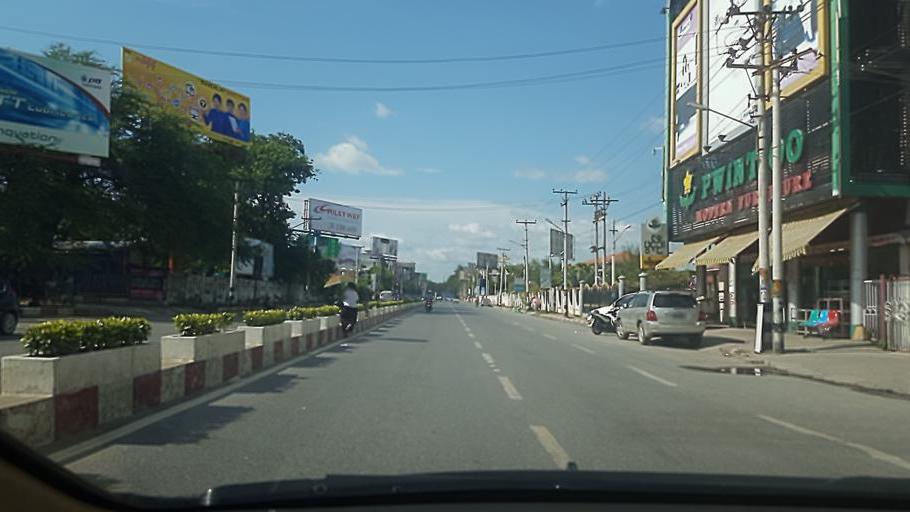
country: MM
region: Mandalay
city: Mandalay
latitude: 21.9779
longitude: 96.0870
